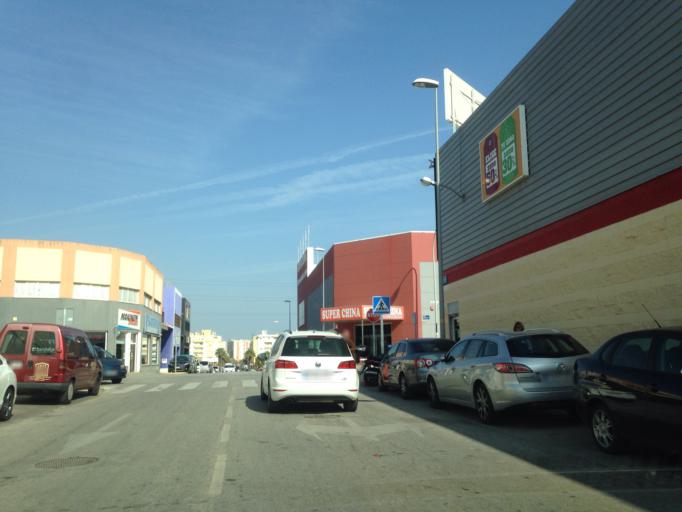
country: ES
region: Andalusia
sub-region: Provincia de Malaga
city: Malaga
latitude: 36.7106
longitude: -4.4693
